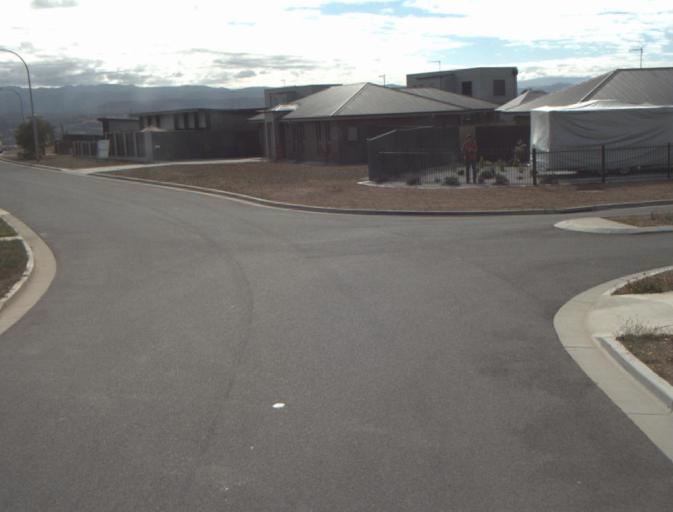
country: AU
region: Tasmania
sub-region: Launceston
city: Summerhill
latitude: -41.4670
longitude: 147.1366
